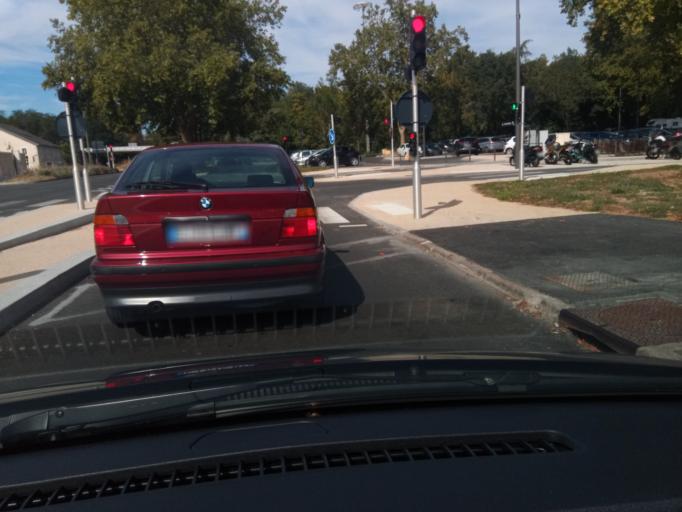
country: FR
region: Poitou-Charentes
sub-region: Departement de la Vienne
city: Poitiers
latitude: 46.5854
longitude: 0.3510
